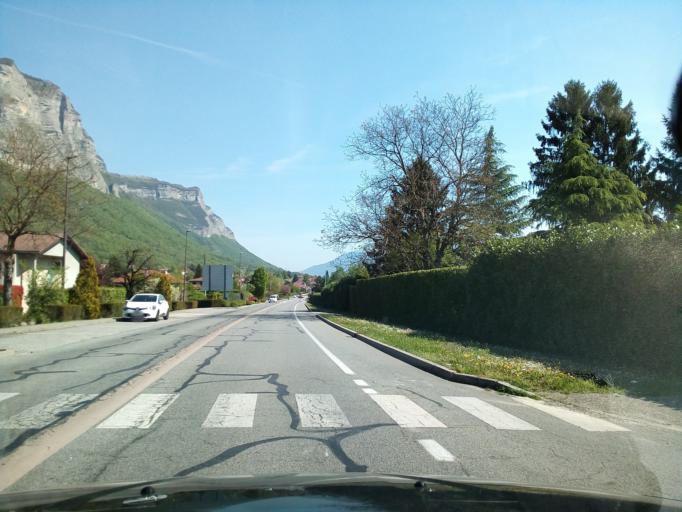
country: FR
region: Rhone-Alpes
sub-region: Departement de l'Isere
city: Crolles
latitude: 45.2774
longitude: 5.8733
